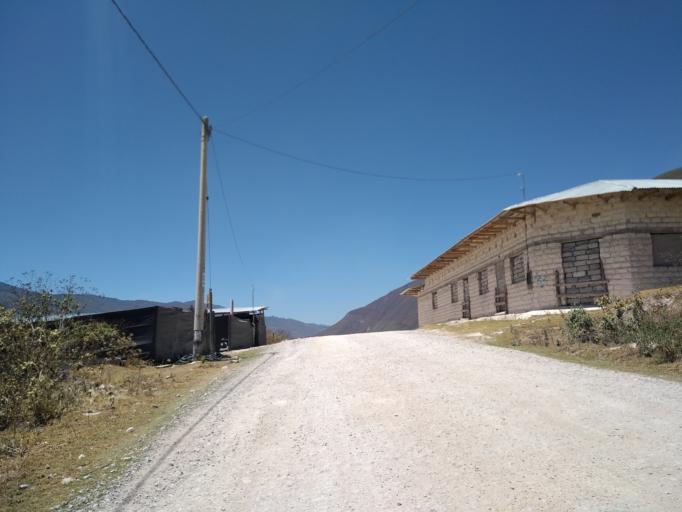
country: PE
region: Amazonas
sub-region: Provincia de Luya
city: Tingo
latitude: -6.3756
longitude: -77.9102
